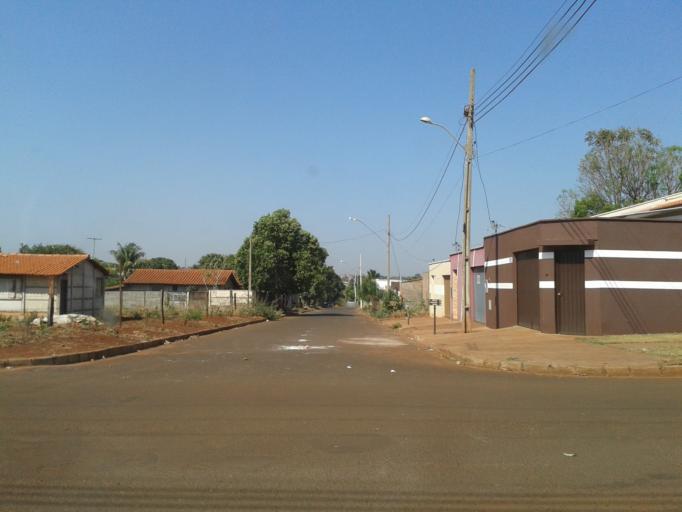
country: BR
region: Minas Gerais
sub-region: Ituiutaba
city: Ituiutaba
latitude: -18.9606
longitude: -49.4820
